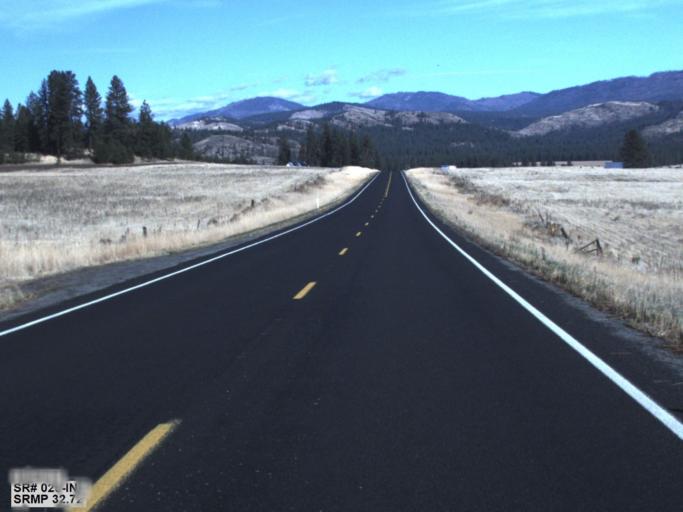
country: US
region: Washington
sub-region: Lincoln County
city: Davenport
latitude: 48.0097
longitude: -118.2559
